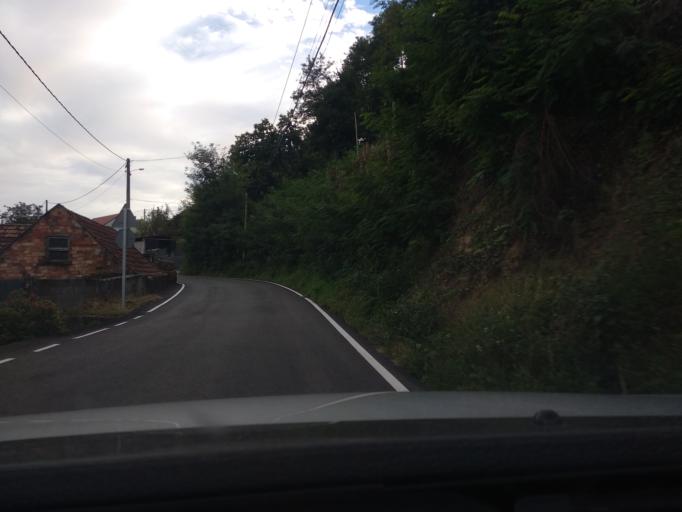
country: ES
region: Galicia
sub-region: Provincia de Pontevedra
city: Moana
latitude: 42.2932
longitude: -8.7388
